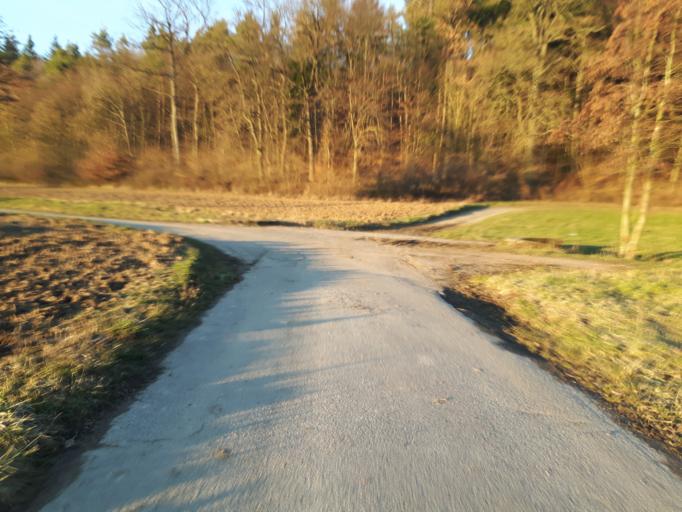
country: DE
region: Baden-Wuerttemberg
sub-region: Regierungsbezirk Stuttgart
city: Massenbachhausen
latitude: 49.1851
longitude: 9.0543
